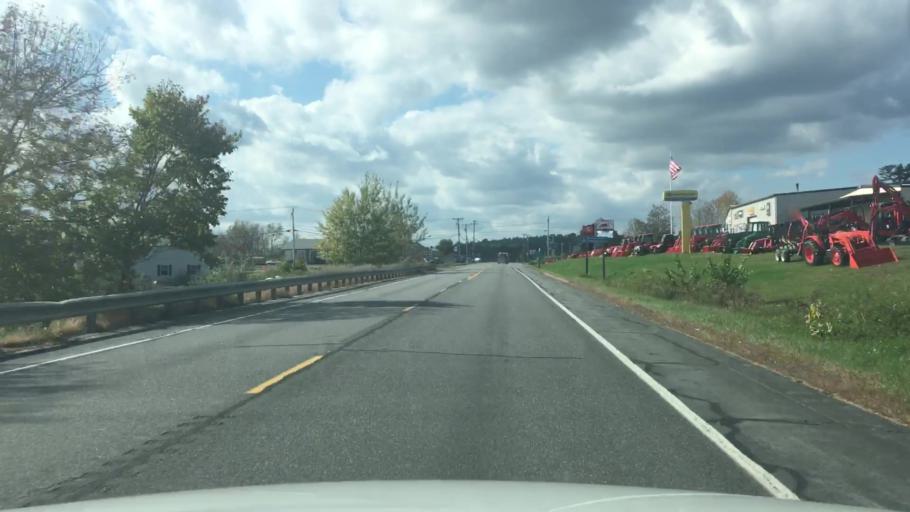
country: US
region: Maine
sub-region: Knox County
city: Union
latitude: 44.2172
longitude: -69.2807
